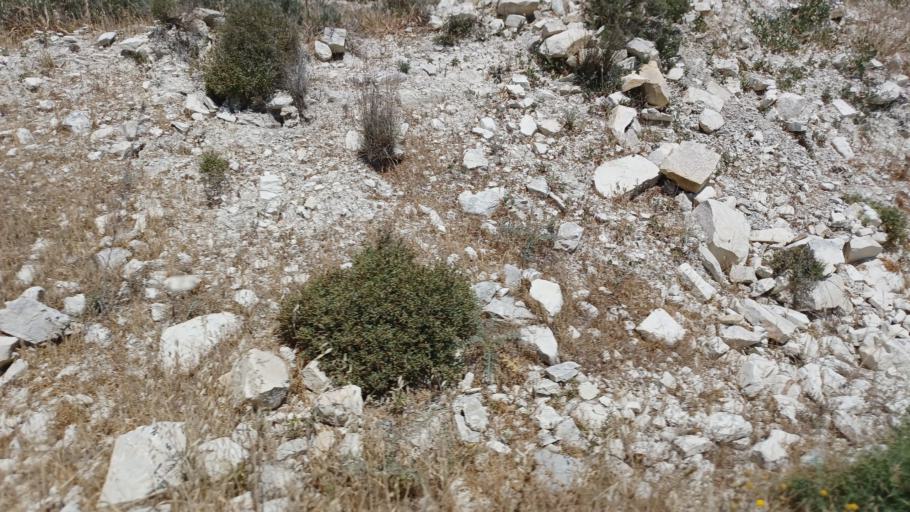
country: CY
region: Larnaka
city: Athienou
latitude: 35.0290
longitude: 33.5375
